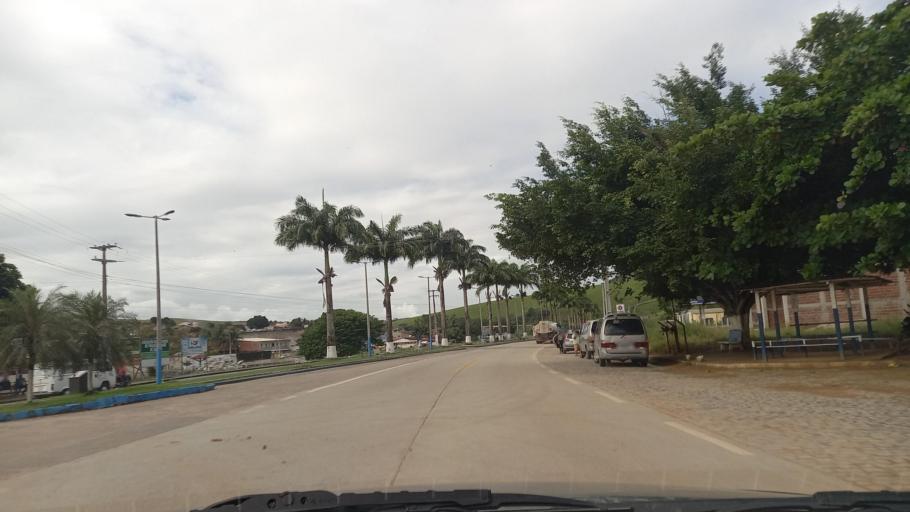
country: BR
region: Pernambuco
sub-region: Maraial
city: Maraial
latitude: -8.7335
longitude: -35.7970
